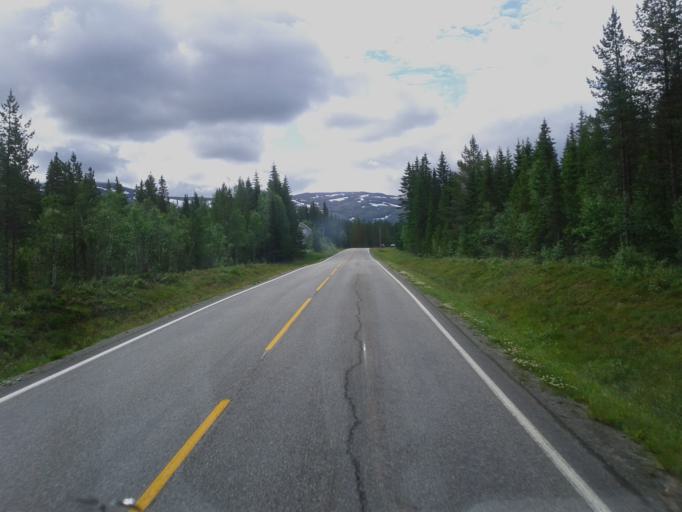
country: NO
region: Nord-Trondelag
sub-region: Hoylandet
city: Hoylandet
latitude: 64.6572
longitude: 12.6491
